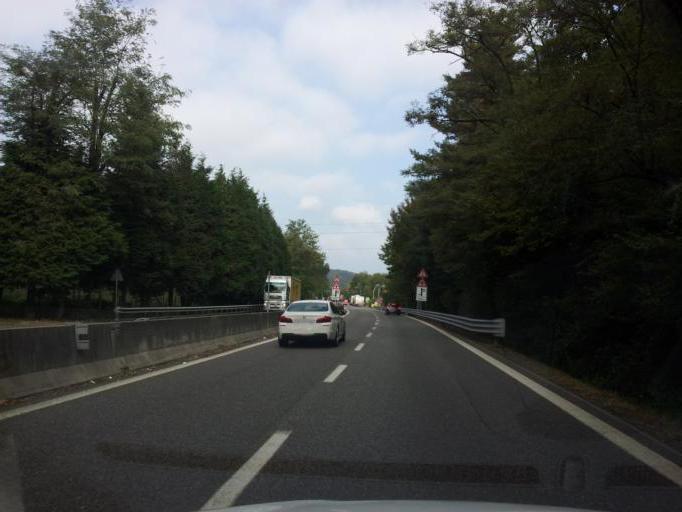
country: IT
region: Lombardy
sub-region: Provincia di Varese
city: Corgeno
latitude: 45.7347
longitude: 8.6798
